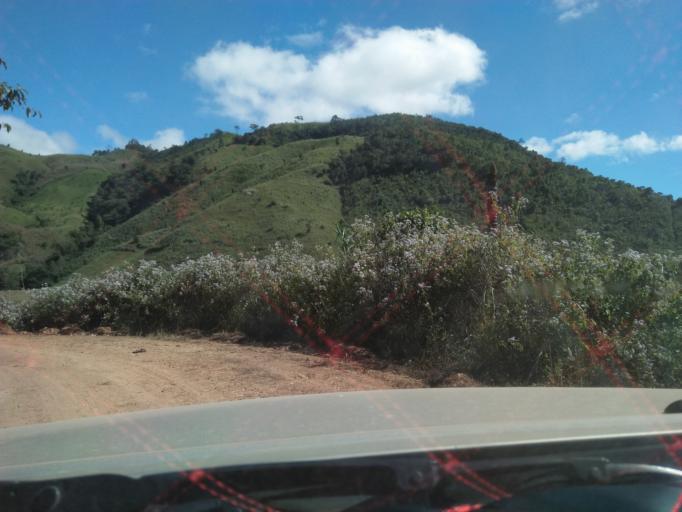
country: TH
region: Nan
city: Chaloem Phra Kiat
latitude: 19.4692
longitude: 101.2784
